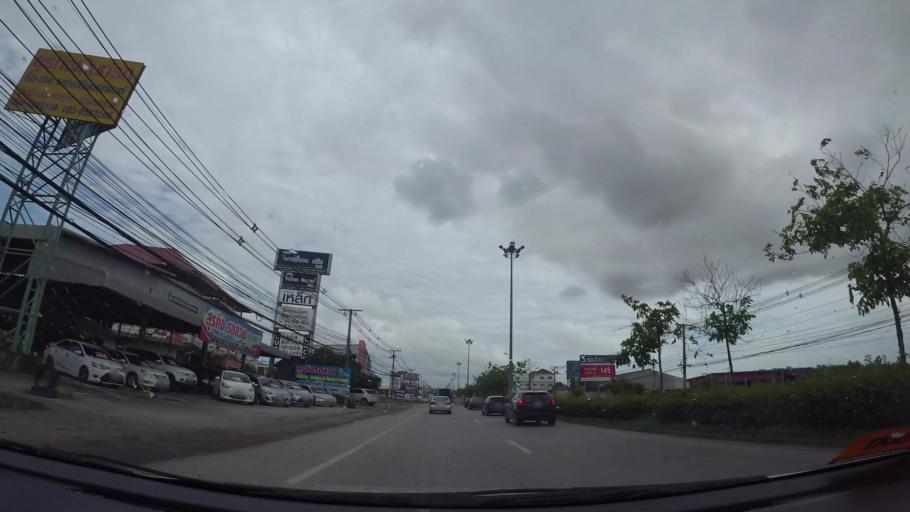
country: TH
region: Rayong
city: Rayong
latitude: 12.6984
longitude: 101.1934
